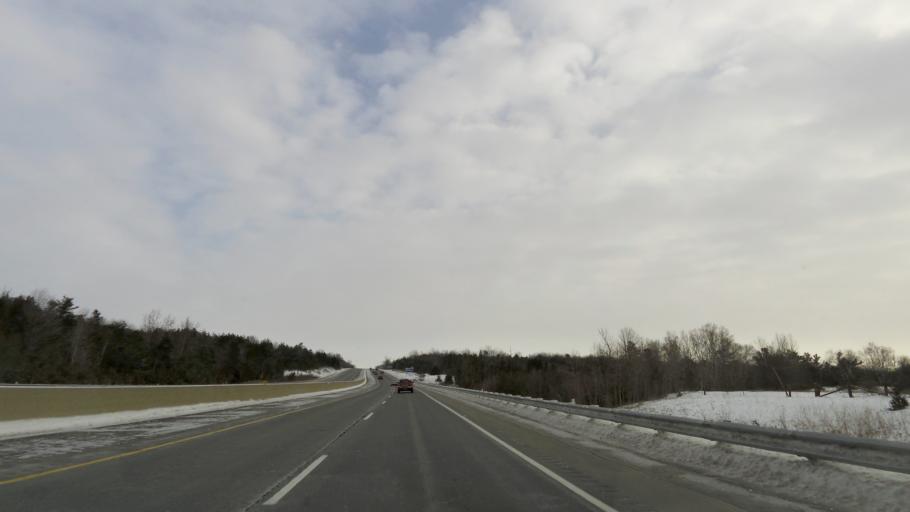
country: CA
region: Ontario
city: Cobourg
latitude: 44.0181
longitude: -77.9331
